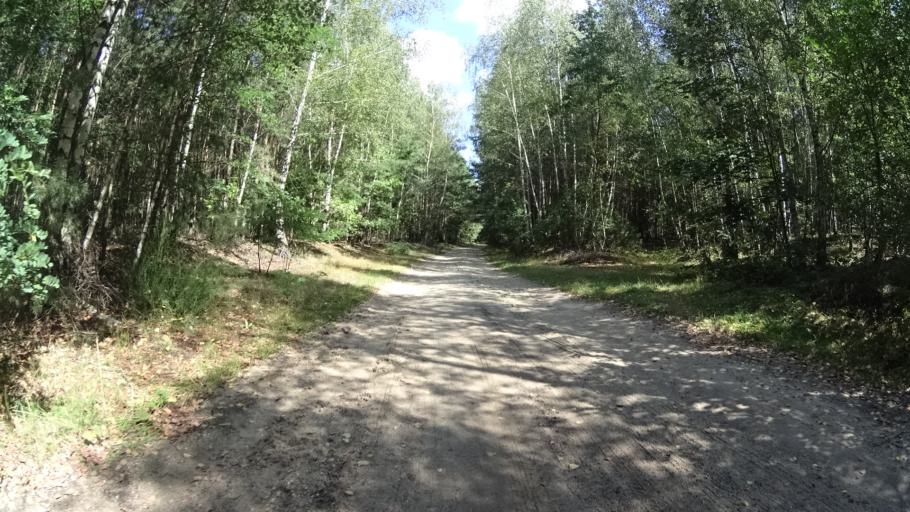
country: PL
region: Masovian Voivodeship
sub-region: Powiat grojecki
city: Mogielnica
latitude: 51.6723
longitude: 20.7474
